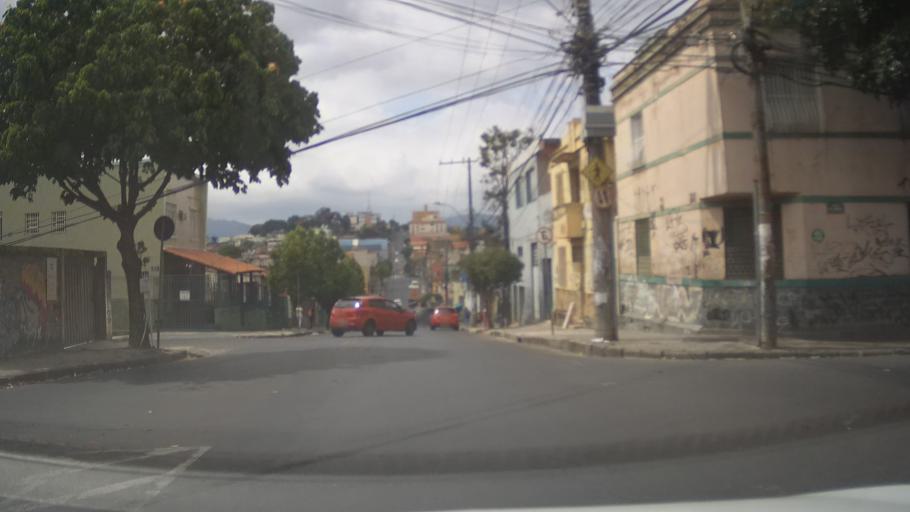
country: BR
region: Minas Gerais
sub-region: Belo Horizonte
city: Belo Horizonte
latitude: -19.8996
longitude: -43.9440
